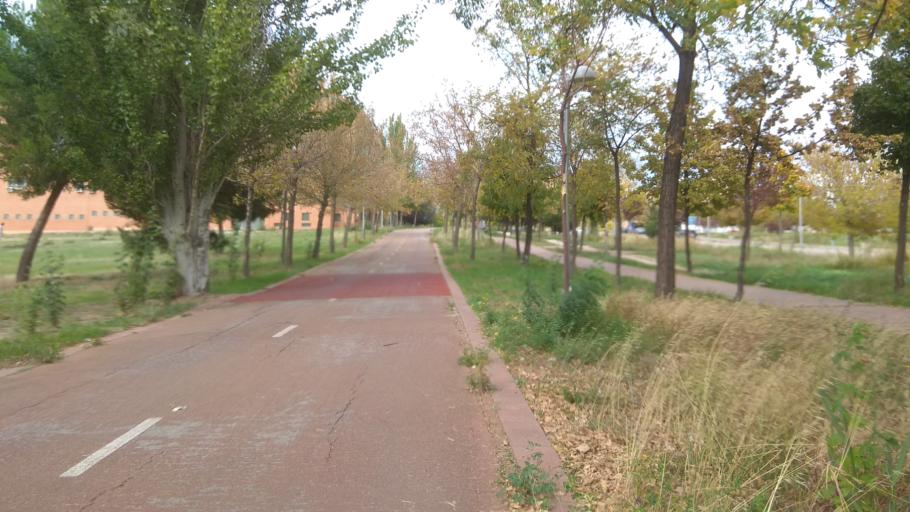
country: ES
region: Madrid
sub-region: Provincia de Madrid
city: San Blas
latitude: 40.4155
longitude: -3.6224
